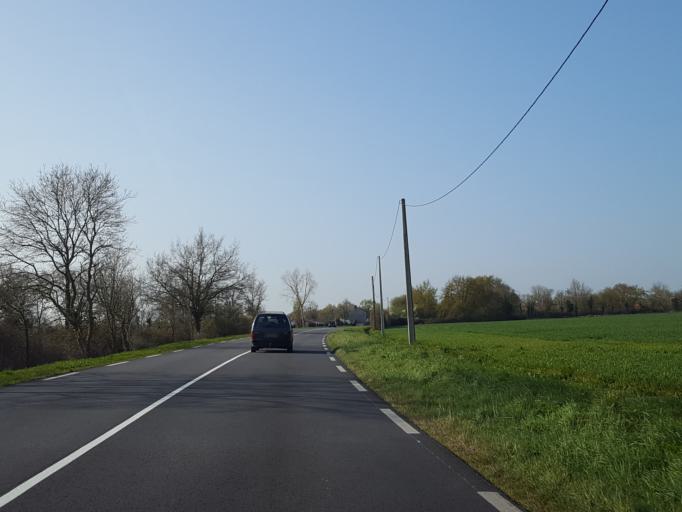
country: FR
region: Pays de la Loire
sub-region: Departement de la Vendee
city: Saint-Philbert-de-Bouaine
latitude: 47.0128
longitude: -1.5040
